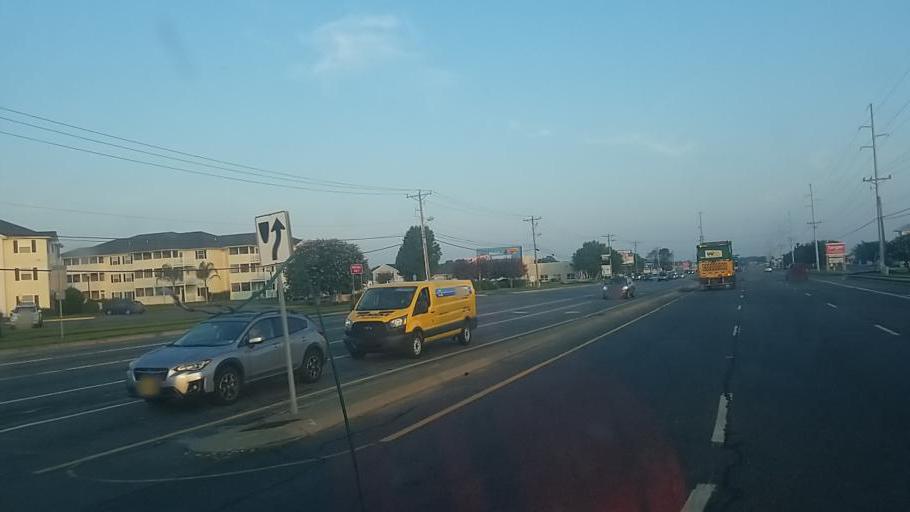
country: US
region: Delaware
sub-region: Sussex County
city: Rehoboth Beach
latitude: 38.7180
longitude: -75.1133
